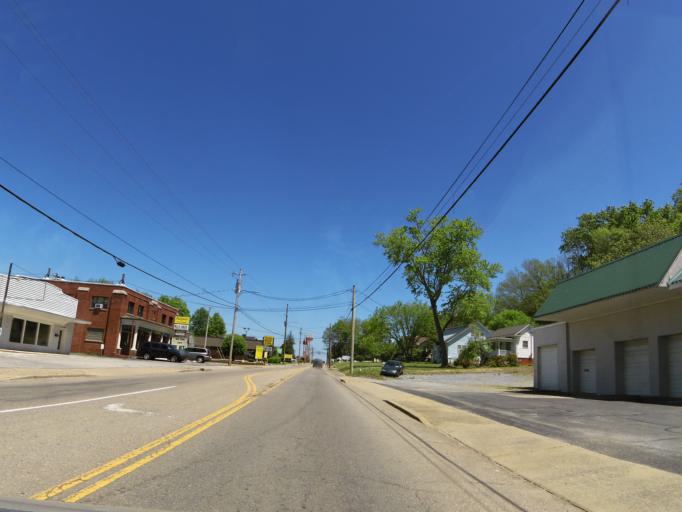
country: US
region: Tennessee
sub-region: Greene County
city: Greeneville
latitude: 36.1679
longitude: -82.8227
